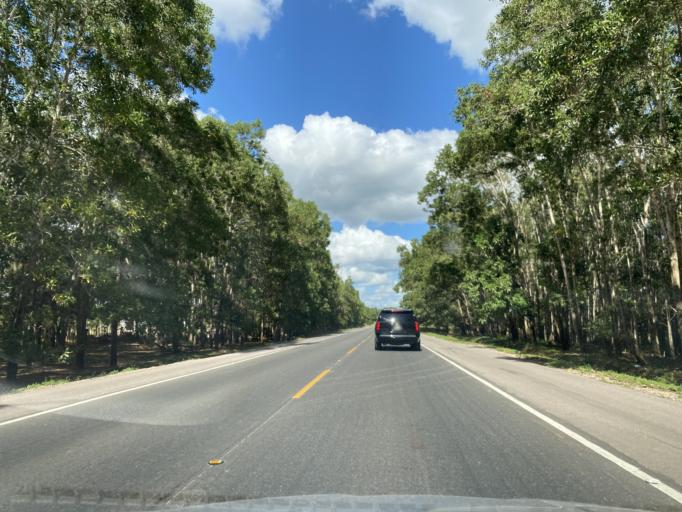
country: DO
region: Monte Plata
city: Monte Plata
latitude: 18.7536
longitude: -69.7654
